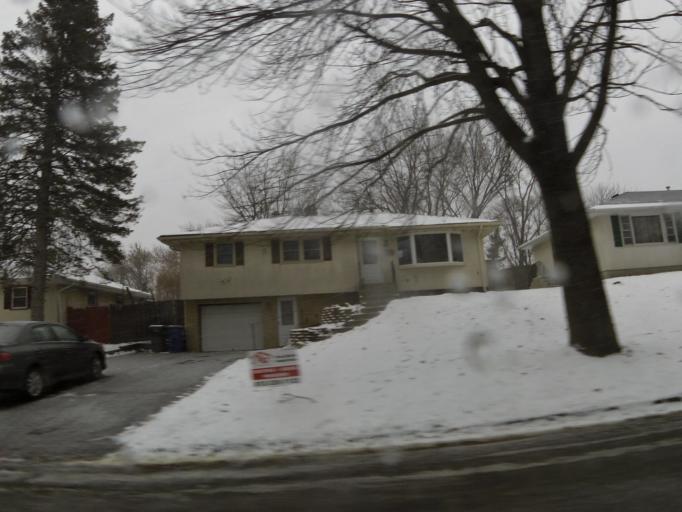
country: US
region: Minnesota
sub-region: Ramsey County
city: Maplewood
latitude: 44.9476
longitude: -93.0280
